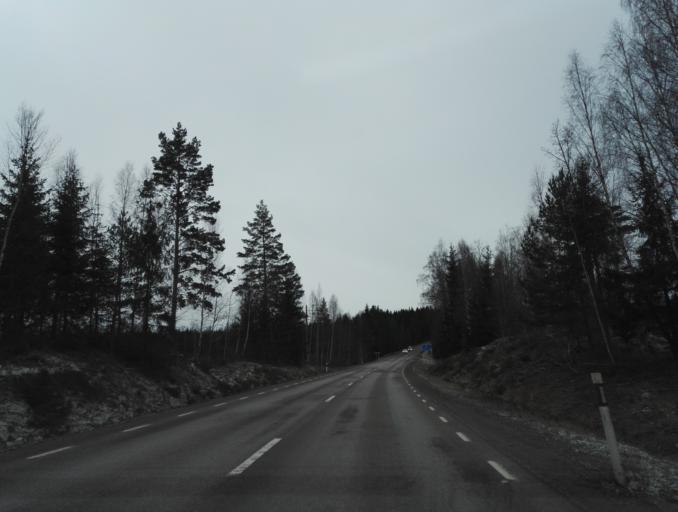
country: SE
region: Kalmar
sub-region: Hultsfreds Kommun
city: Virserum
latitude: 57.3057
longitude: 15.5839
